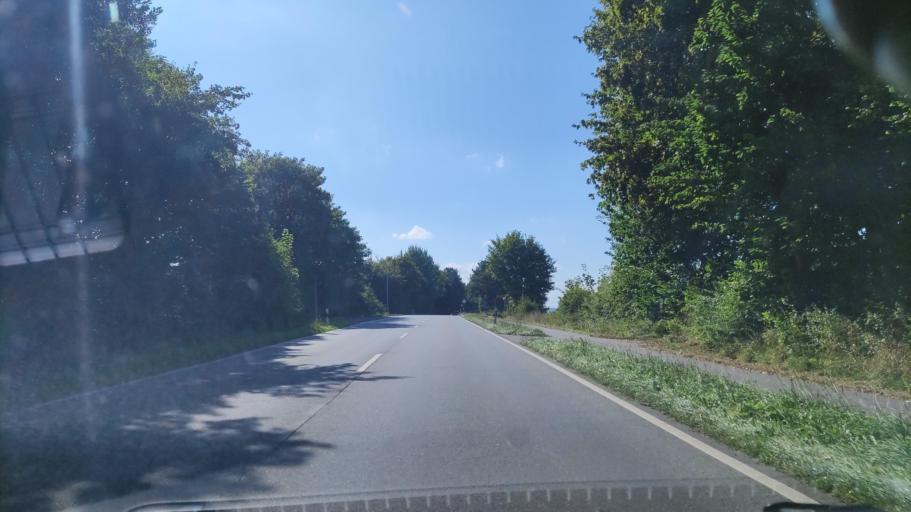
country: DE
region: Schleswig-Holstein
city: Windeby
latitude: 54.4600
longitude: 9.7855
